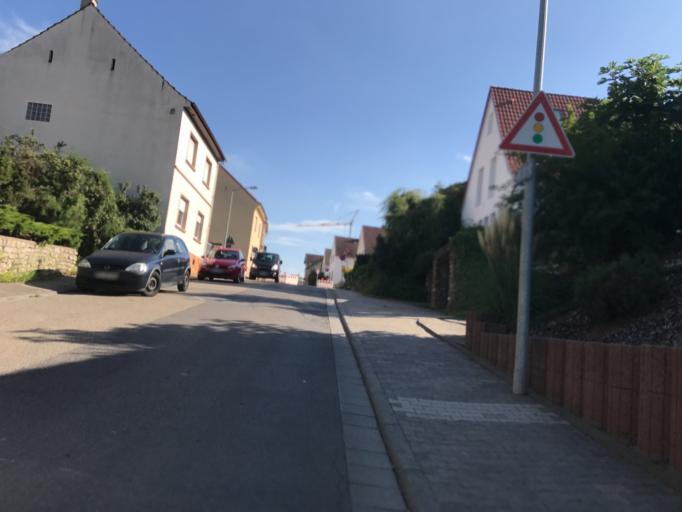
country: DE
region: Rheinland-Pfalz
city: Wackernheim
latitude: 49.9764
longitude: 8.1185
